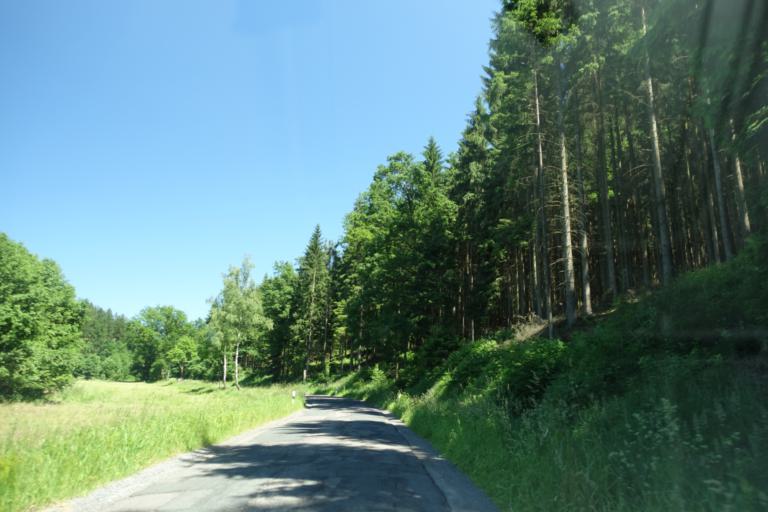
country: DE
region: Saxony
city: Leubsdorf
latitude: 50.8157
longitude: 13.1945
